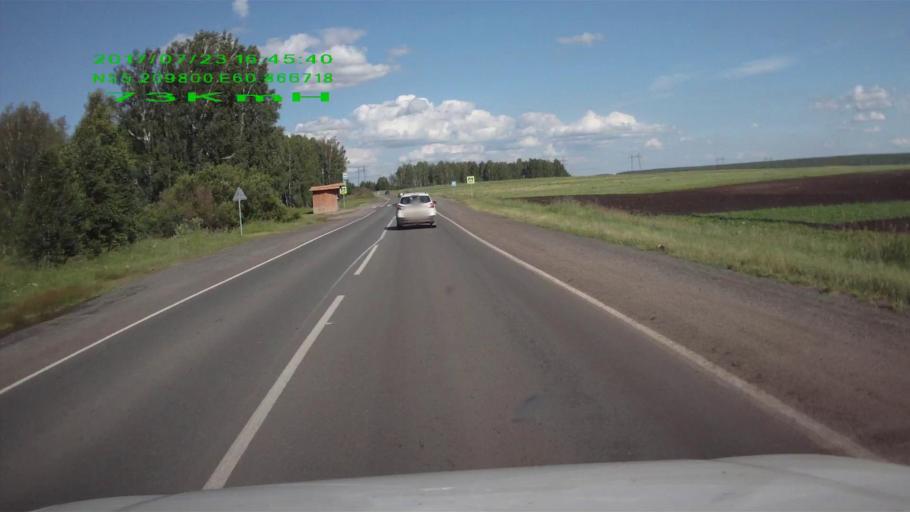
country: RU
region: Chelyabinsk
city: Argayash
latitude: 55.2098
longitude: 60.8666
